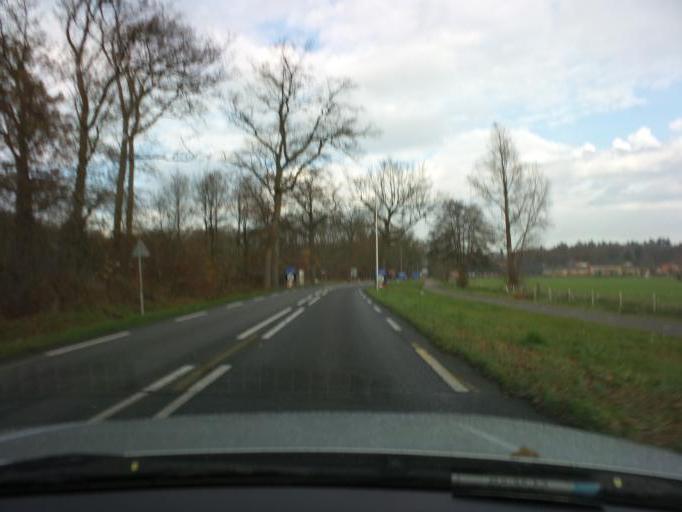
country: NL
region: Utrecht
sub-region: Gemeente Amersfoort
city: Randenbroek
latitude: 52.1285
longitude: 5.3984
